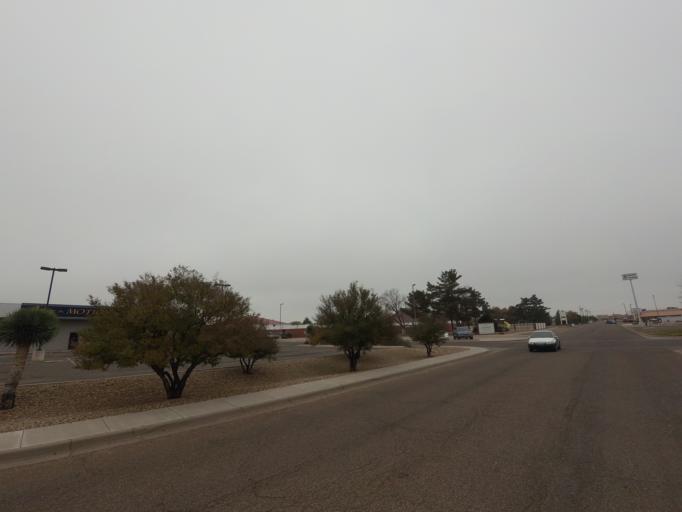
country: US
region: New Mexico
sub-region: Curry County
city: Clovis
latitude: 34.4234
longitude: -103.1946
